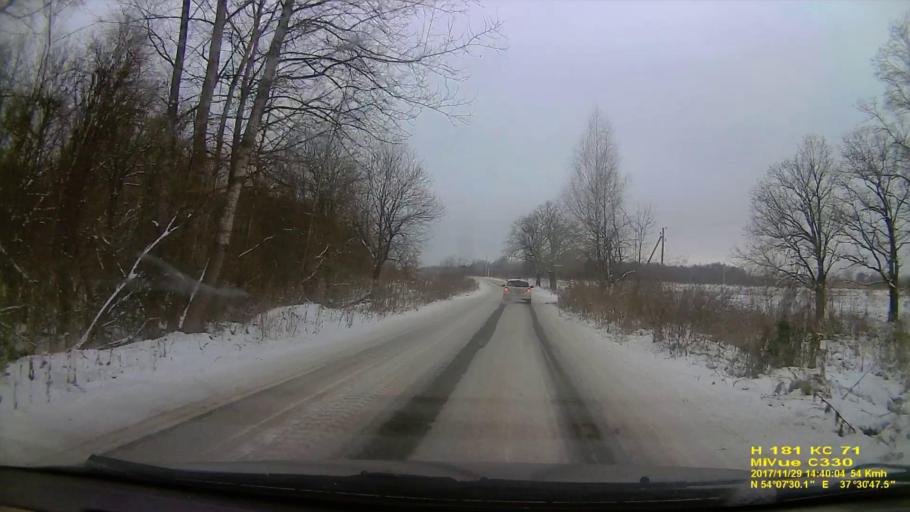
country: RU
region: Tula
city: Kosaya Gora
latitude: 54.1249
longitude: 37.5130
